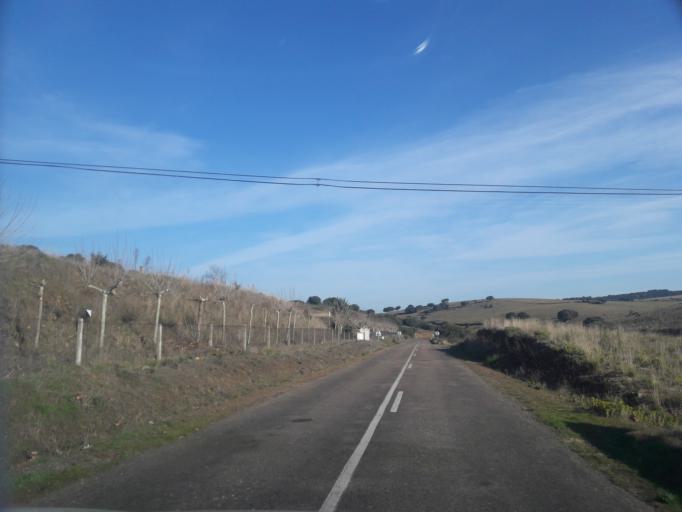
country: ES
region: Castille and Leon
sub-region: Provincia de Salamanca
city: Salvatierra de Tormes
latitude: 40.5886
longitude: -5.6043
